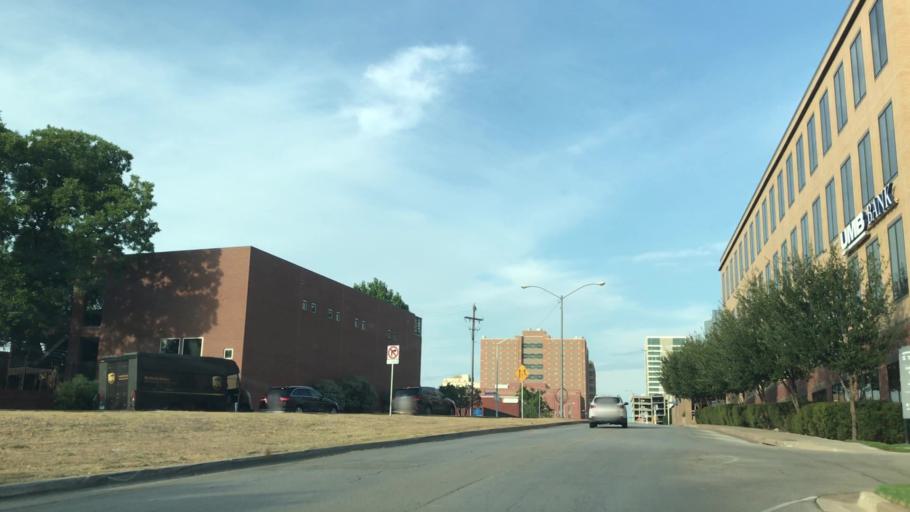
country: US
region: Texas
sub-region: Tarrant County
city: Fort Worth
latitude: 32.7530
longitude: -97.3414
